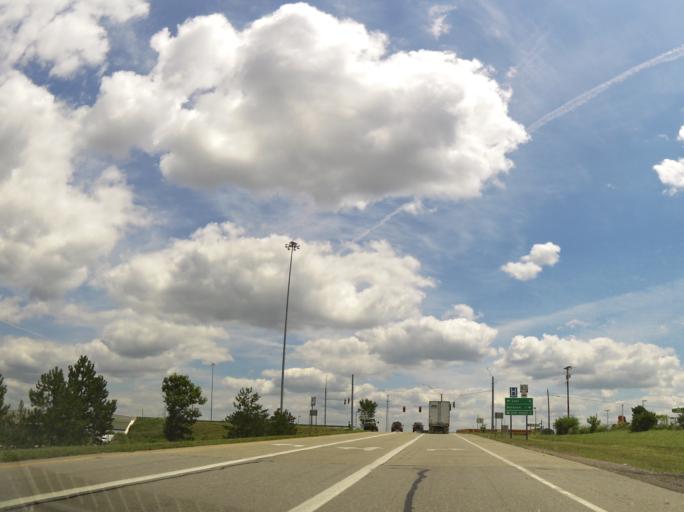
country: US
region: Ohio
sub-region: Medina County
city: Lodi
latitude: 40.9969
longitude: -81.9977
